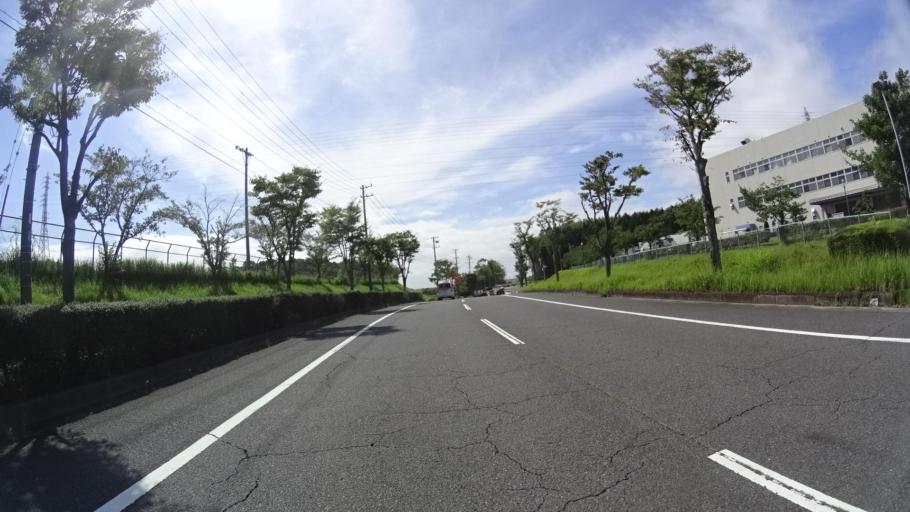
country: JP
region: Mie
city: Kawage
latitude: 34.8352
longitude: 136.5393
